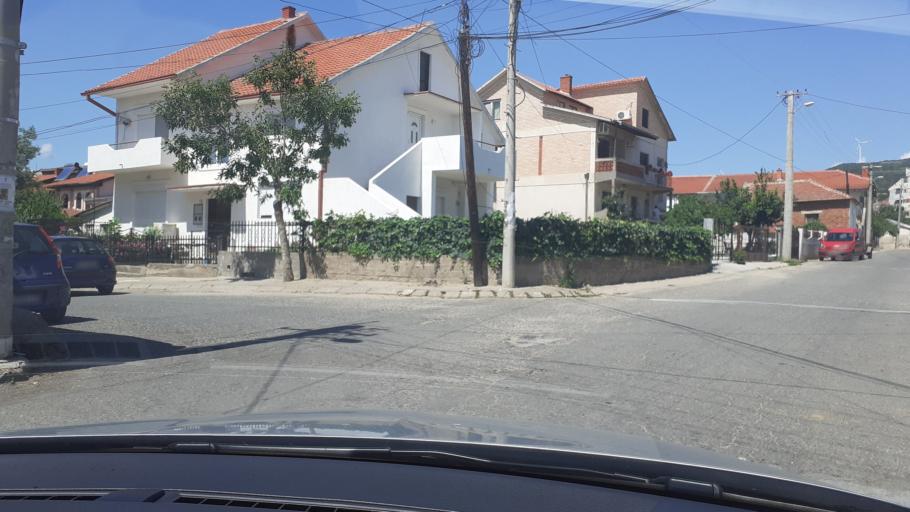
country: MK
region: Bogdanci
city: Bogdanci
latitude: 41.1999
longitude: 22.5744
